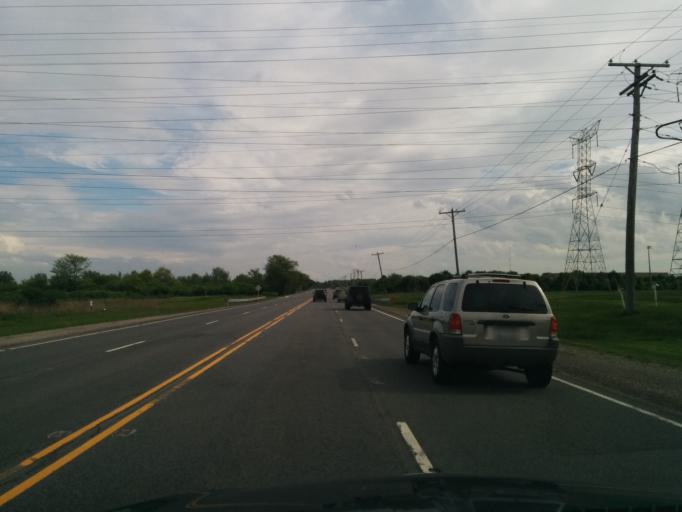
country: US
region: Illinois
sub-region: Will County
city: Romeoville
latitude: 41.6329
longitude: -88.0804
